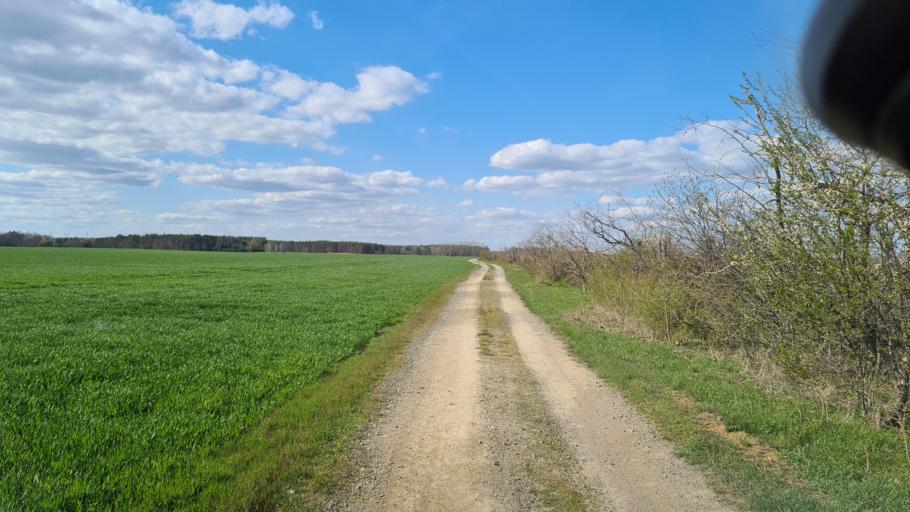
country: DE
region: Brandenburg
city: Falkenberg
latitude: 51.5163
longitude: 13.2742
